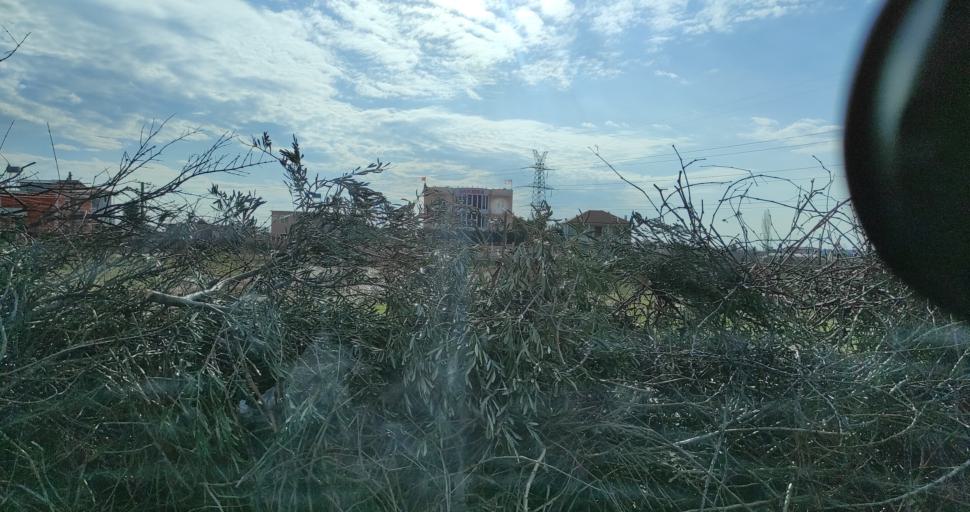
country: AL
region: Lezhe
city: Lezhe
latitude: 41.7842
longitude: 19.6291
